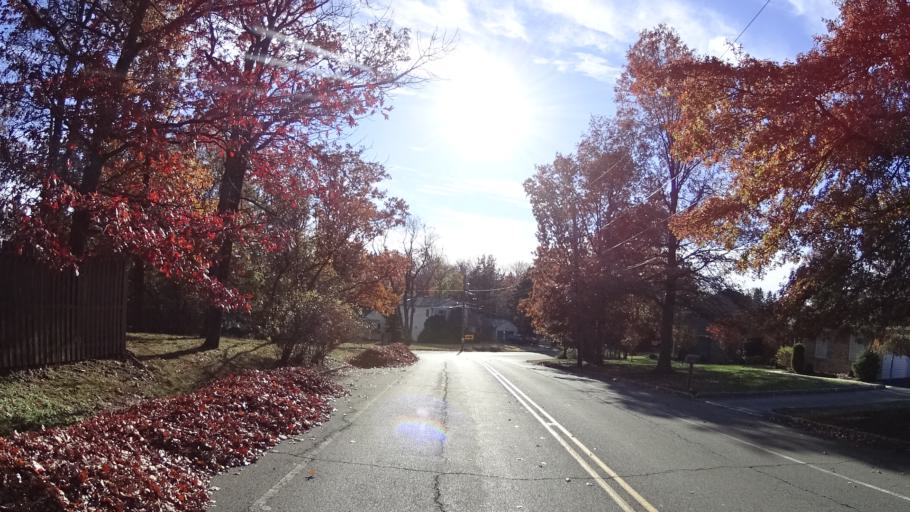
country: US
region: New Jersey
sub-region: Union County
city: Mountainside
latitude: 40.6830
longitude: -74.3692
